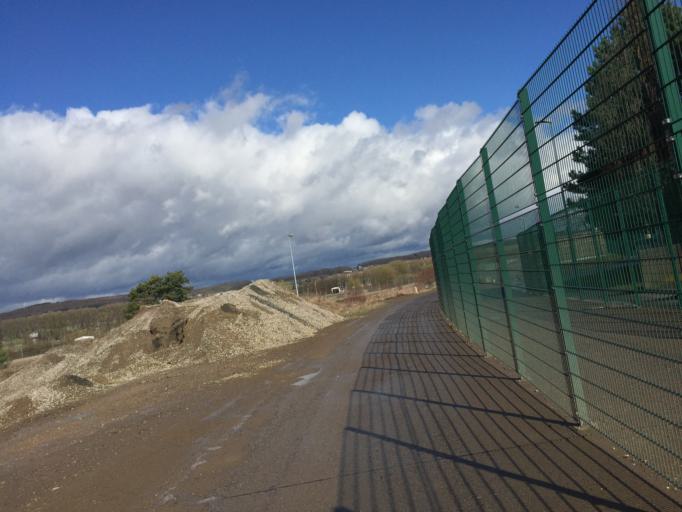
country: DE
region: Hesse
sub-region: Regierungsbezirk Giessen
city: Alten Buseck
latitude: 50.5968
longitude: 8.7324
